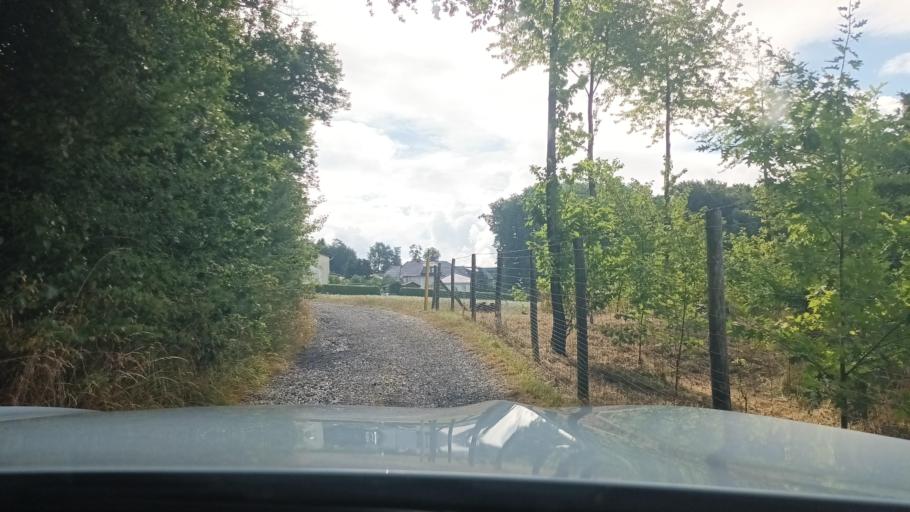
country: DE
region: North Rhine-Westphalia
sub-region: Regierungsbezirk Koln
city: Hennef
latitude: 50.7405
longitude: 7.3501
